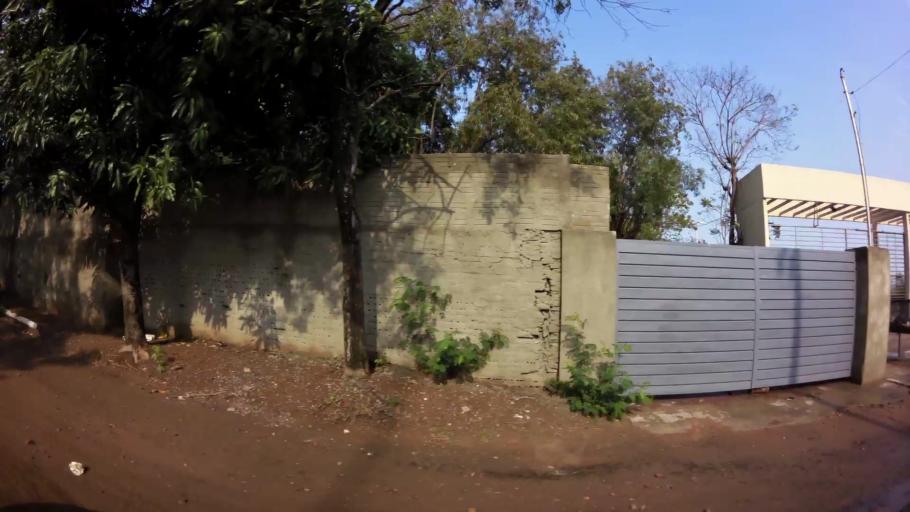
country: PY
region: Presidente Hayes
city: Nanawa
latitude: -25.2761
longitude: -57.6478
